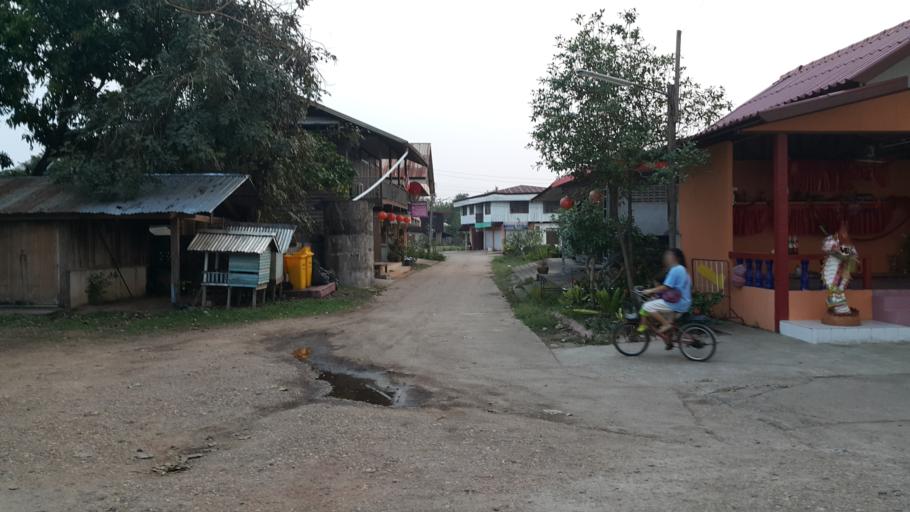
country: LA
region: Khammouan
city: Muang Hinboun
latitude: 17.6533
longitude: 104.4640
